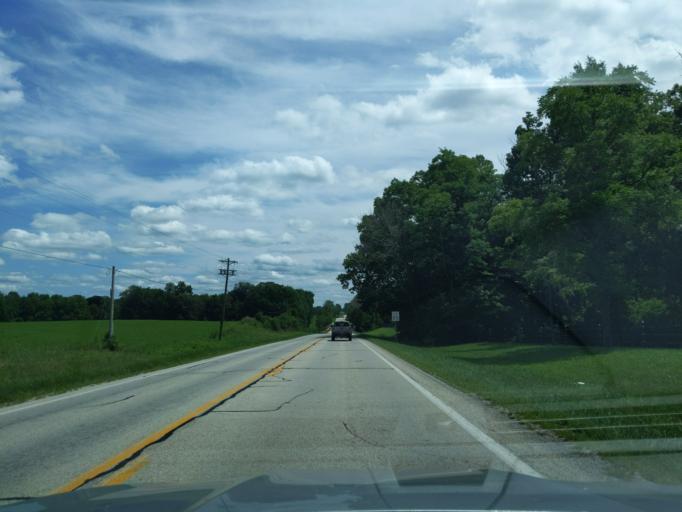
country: US
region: Indiana
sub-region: Ripley County
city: Batesville
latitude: 39.3091
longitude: -85.3063
